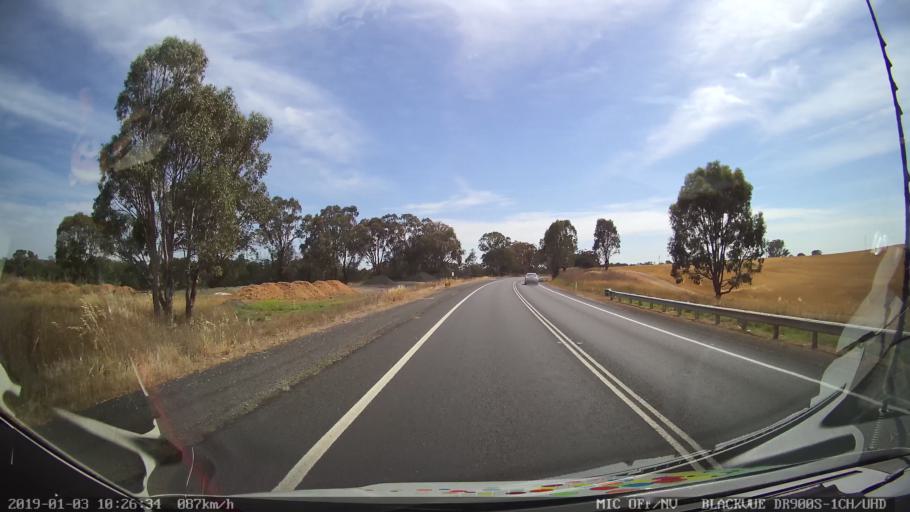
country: AU
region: New South Wales
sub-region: Young
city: Young
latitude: -34.4112
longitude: 148.2502
